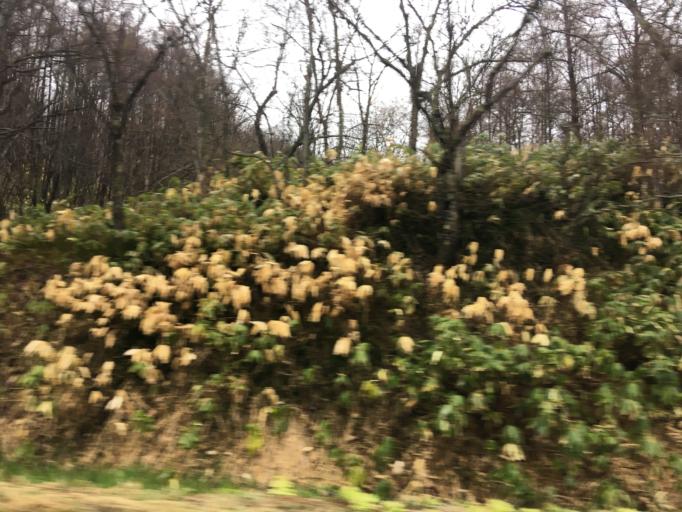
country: JP
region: Hokkaido
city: Nayoro
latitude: 44.0792
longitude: 142.4196
